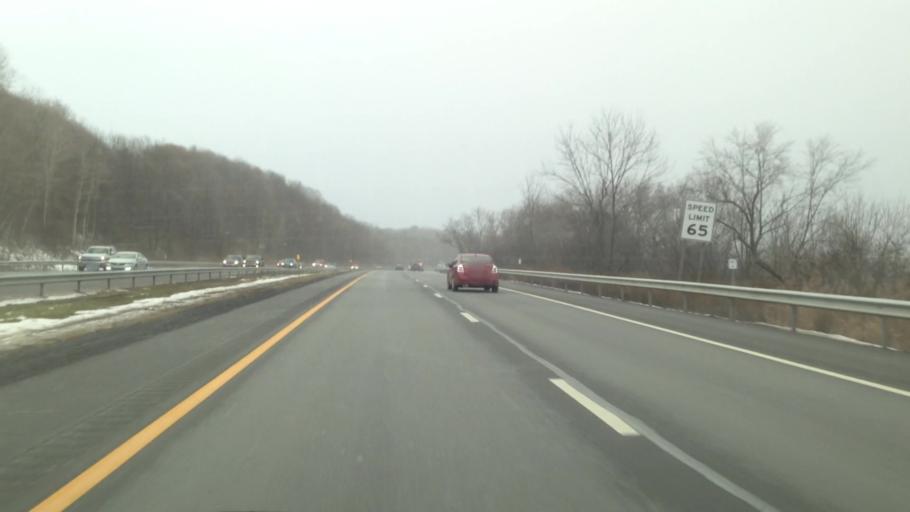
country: US
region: New York
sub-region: Schenectady County
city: Scotia
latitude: 42.8740
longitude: -74.0561
